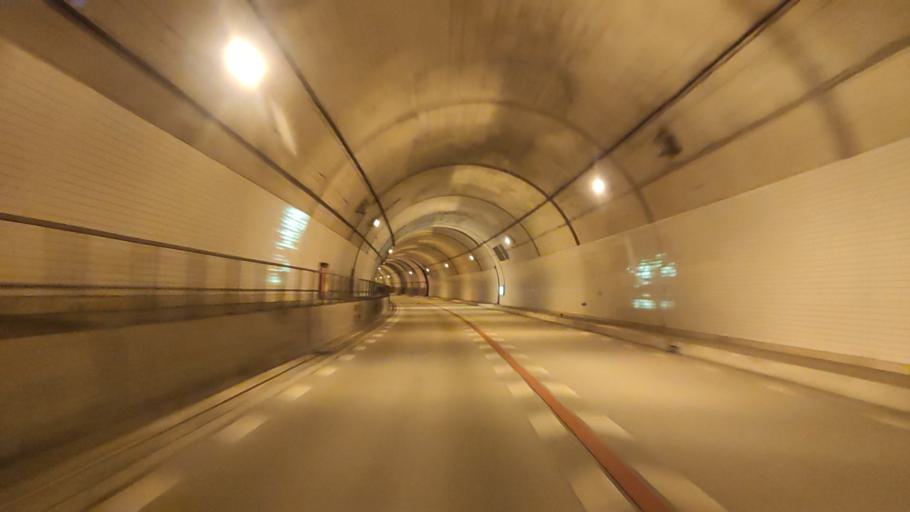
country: JP
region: Hyogo
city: Akashi
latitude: 34.6702
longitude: 135.0584
